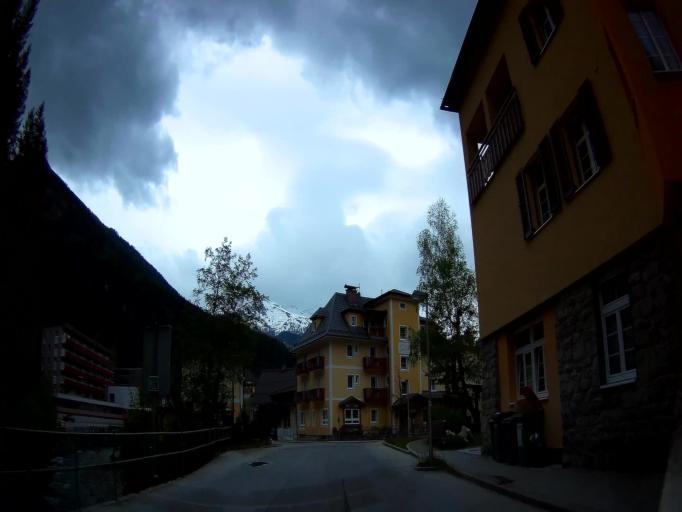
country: AT
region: Salzburg
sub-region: Politischer Bezirk Sankt Johann im Pongau
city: Bad Gastein
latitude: 47.1099
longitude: 13.1364
